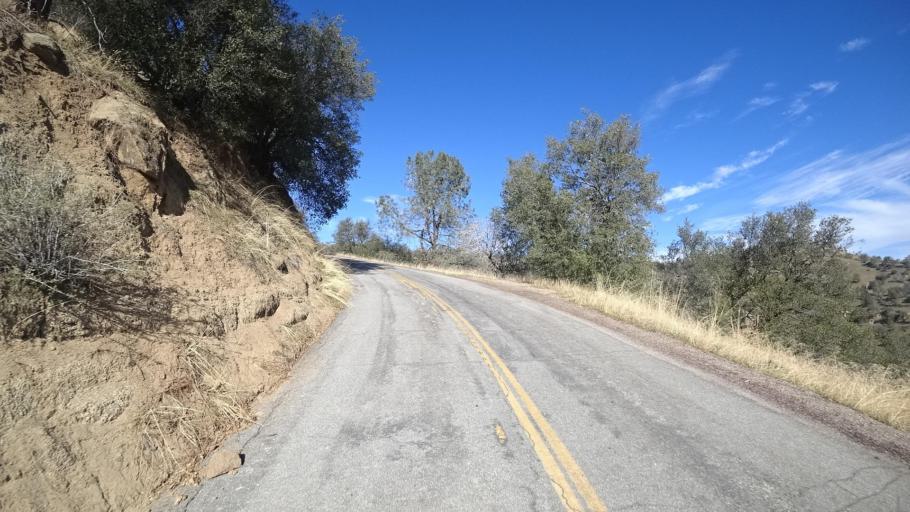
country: US
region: California
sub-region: Kern County
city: Alta Sierra
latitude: 35.6320
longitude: -118.7580
